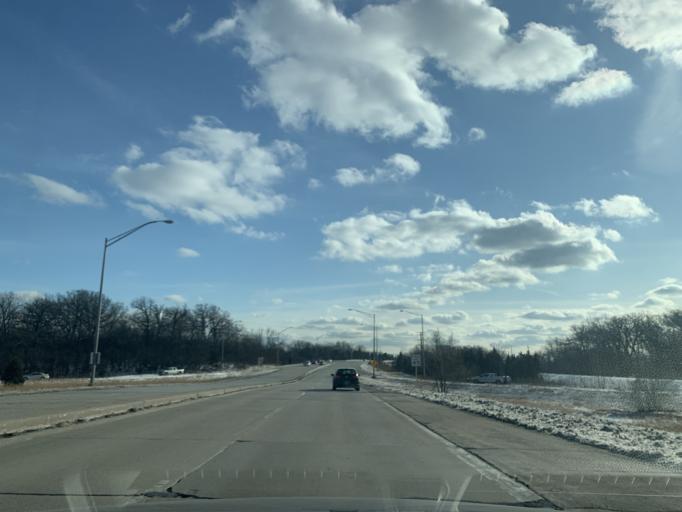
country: US
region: Illinois
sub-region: DuPage County
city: Oak Brook
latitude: 41.8607
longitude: -87.9306
